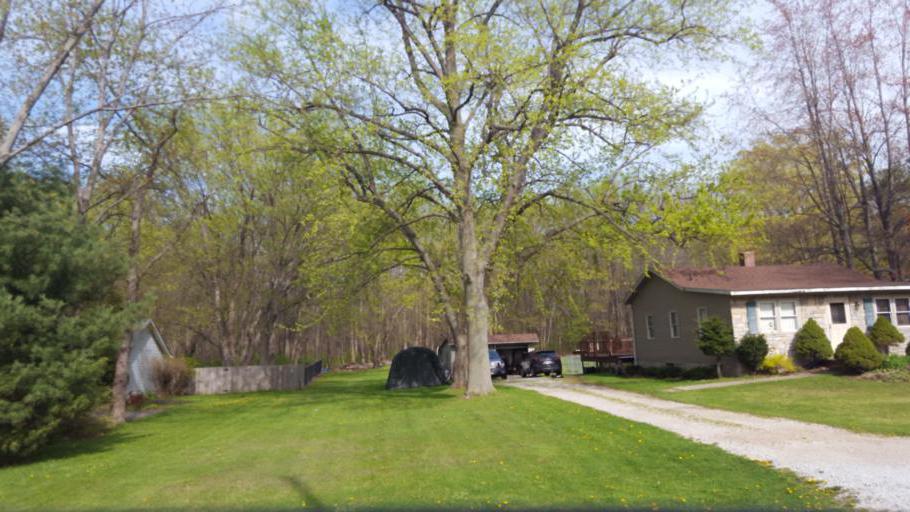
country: US
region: Ohio
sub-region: Lake County
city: North Madison
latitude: 41.8275
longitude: -81.0618
